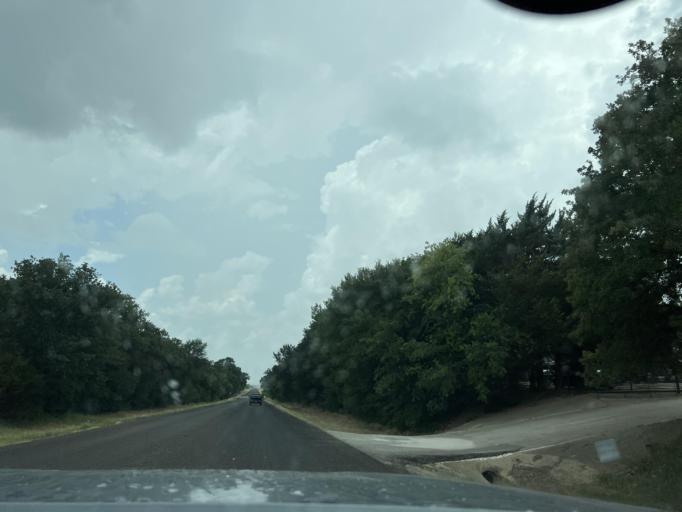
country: US
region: Texas
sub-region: Wise County
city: Decatur
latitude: 33.1521
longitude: -97.6347
